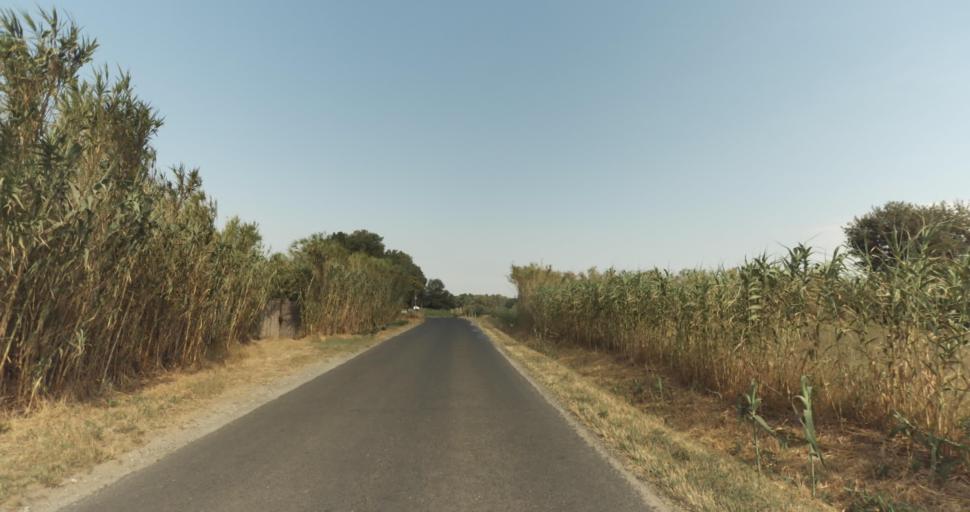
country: FR
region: Languedoc-Roussillon
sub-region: Departement des Pyrenees-Orientales
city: Latour-Bas-Elne
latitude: 42.5970
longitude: 3.0159
